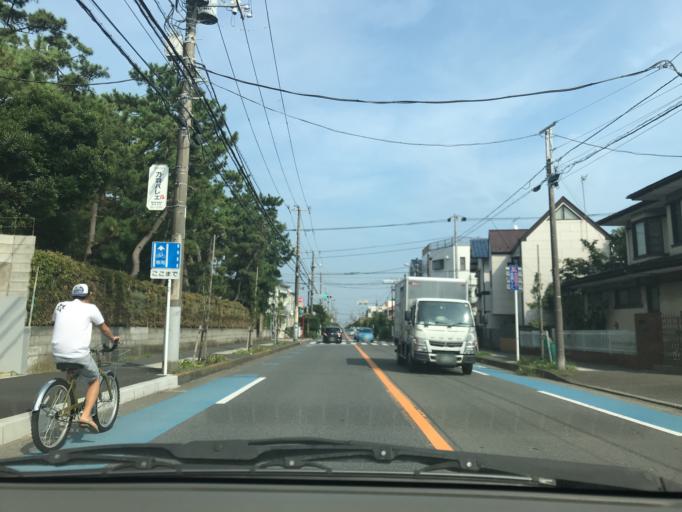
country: JP
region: Kanagawa
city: Chigasaki
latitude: 35.3252
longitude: 139.4190
